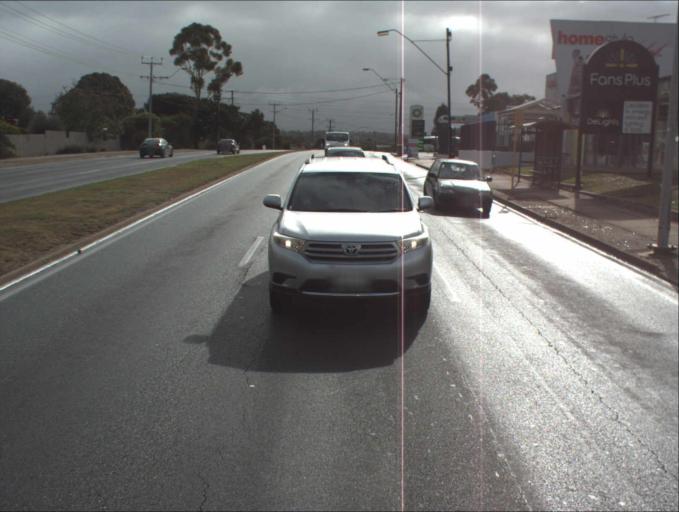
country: AU
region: South Australia
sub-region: Tea Tree Gully
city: Modbury
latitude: -34.8473
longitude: 138.6701
